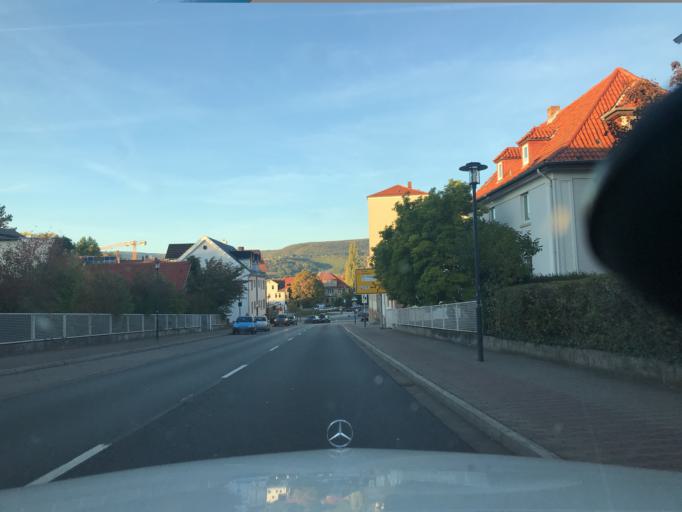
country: DE
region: Hesse
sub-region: Regierungsbezirk Kassel
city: Eschwege
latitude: 51.1901
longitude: 10.0436
